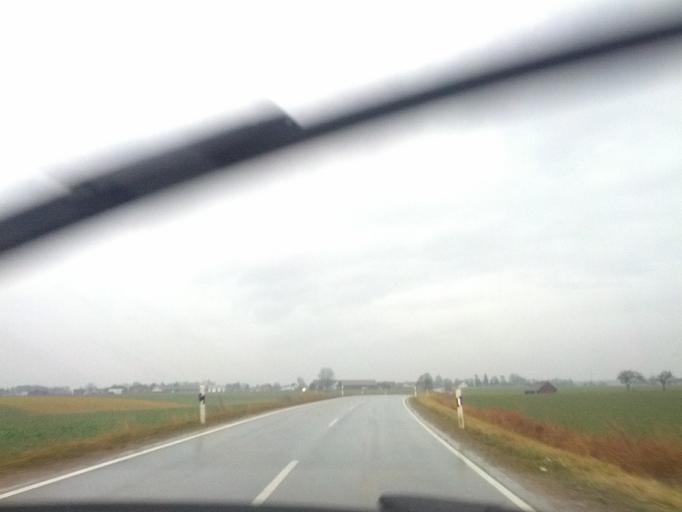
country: DE
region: Baden-Wuerttemberg
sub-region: Tuebingen Region
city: Rot an der Rot
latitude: 48.0323
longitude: 10.0180
